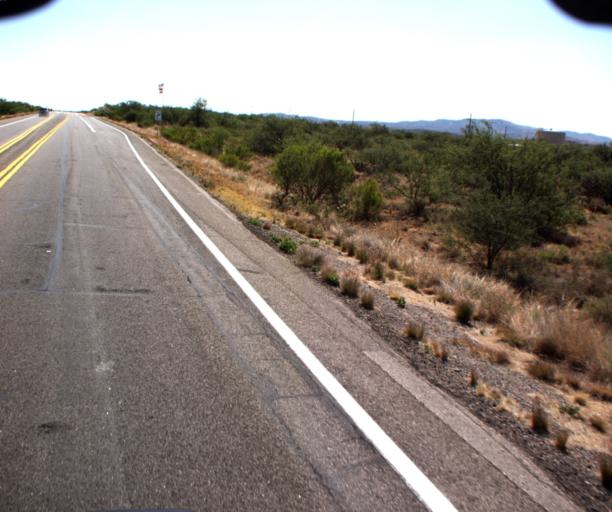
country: US
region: Arizona
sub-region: Pinal County
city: Oracle
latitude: 32.6037
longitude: -110.8636
